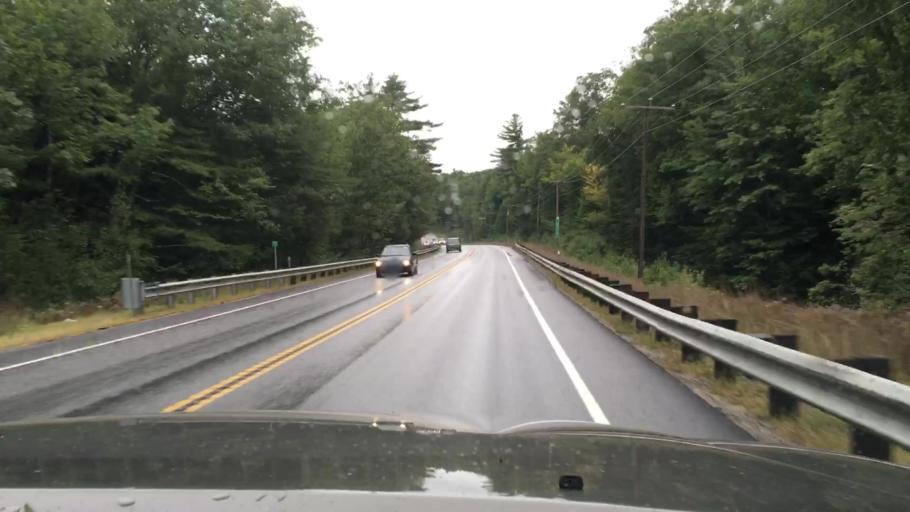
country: US
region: New Hampshire
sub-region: Hillsborough County
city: Hillsborough
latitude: 43.0956
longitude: -71.9641
